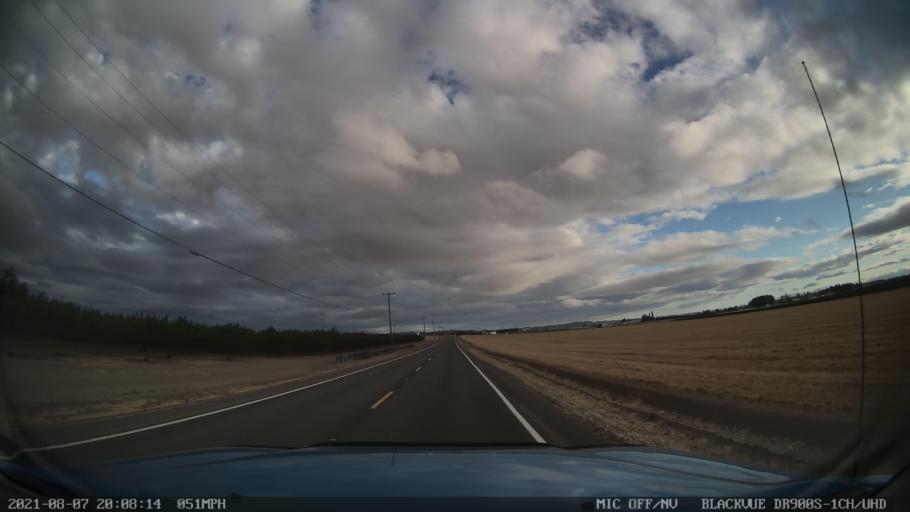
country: US
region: Oregon
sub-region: Marion County
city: Silverton
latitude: 44.9832
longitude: -122.8805
